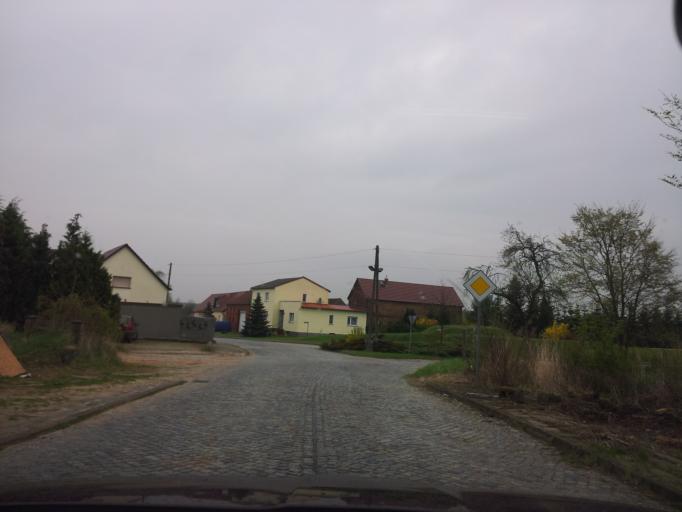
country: DE
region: Brandenburg
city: Niedergorsdorf
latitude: 52.0096
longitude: 12.9214
